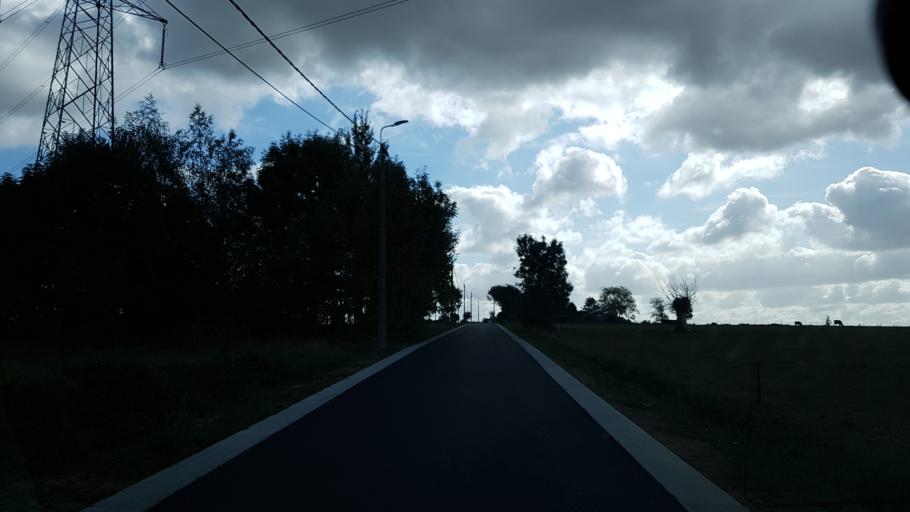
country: BE
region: Wallonia
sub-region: Province de Liege
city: Huy
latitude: 50.4846
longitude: 5.1865
